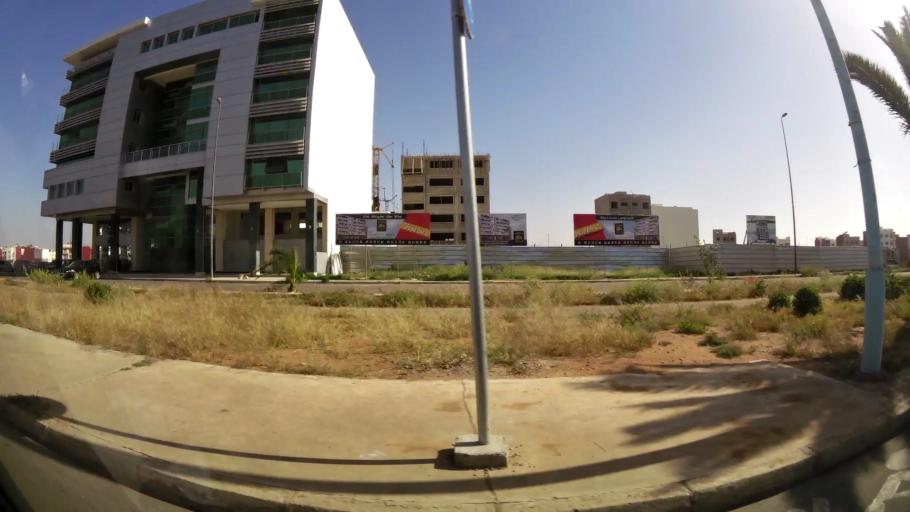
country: MA
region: Oued ed Dahab-Lagouira
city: Dakhla
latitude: 30.4031
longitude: -9.5787
